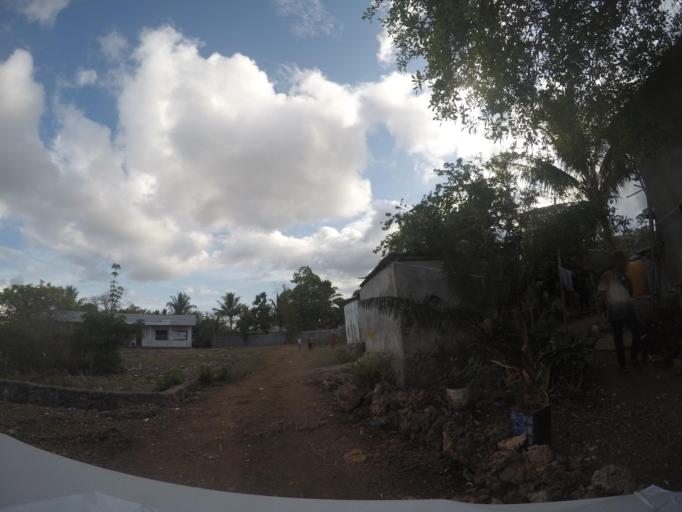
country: TL
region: Baucau
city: Baucau
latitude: -8.4789
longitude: 126.4567
